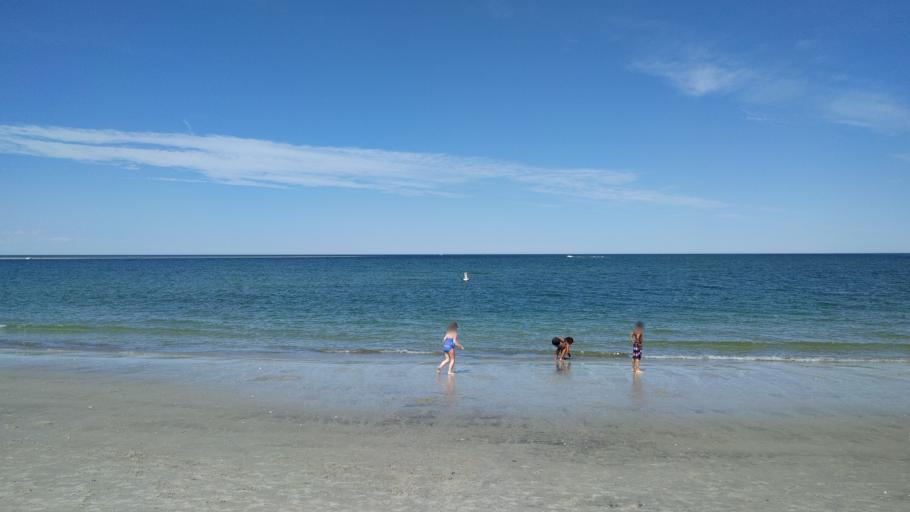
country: US
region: Massachusetts
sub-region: Essex County
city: Essex
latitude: 42.6869
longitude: -70.7659
